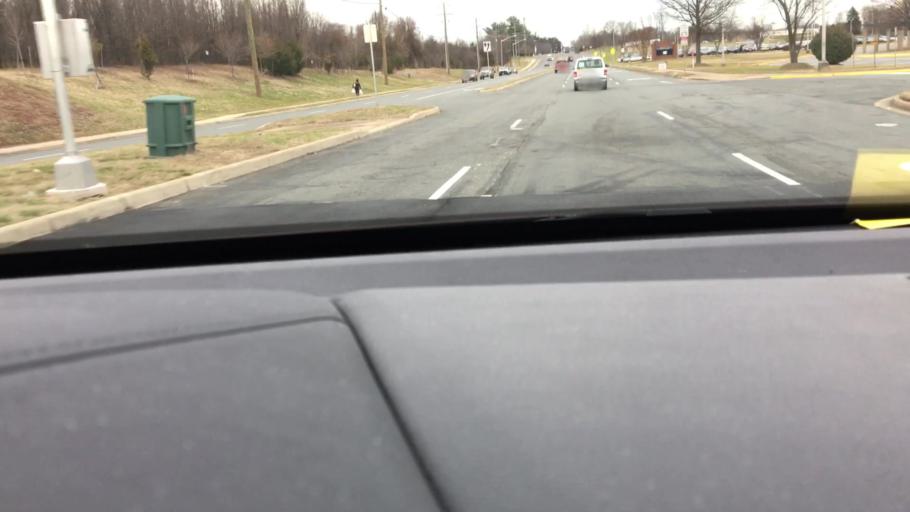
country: US
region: Virginia
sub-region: City of Manassas
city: Manassas
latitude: 38.7629
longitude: -77.4513
